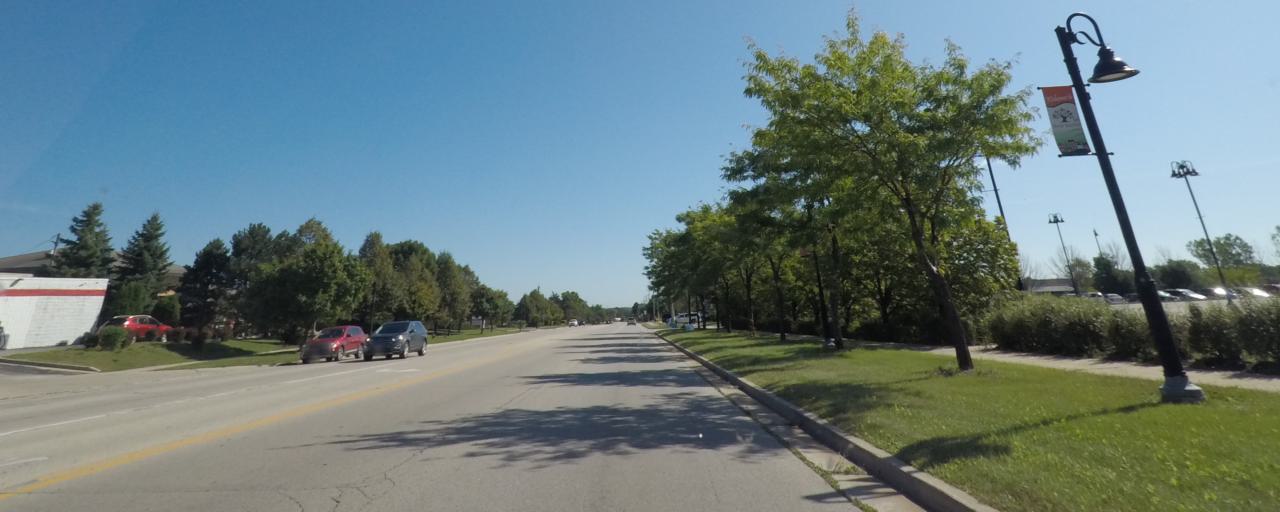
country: US
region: Wisconsin
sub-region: Waukesha County
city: New Berlin
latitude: 42.9857
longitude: -88.0881
